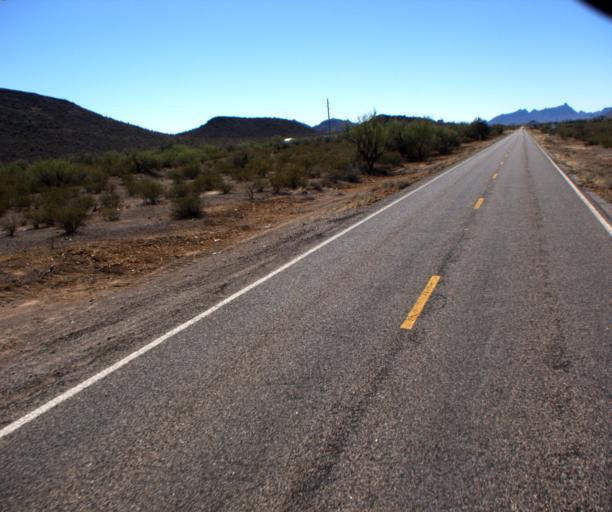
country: US
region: Arizona
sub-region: Pima County
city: Ajo
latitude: 32.2817
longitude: -112.7448
